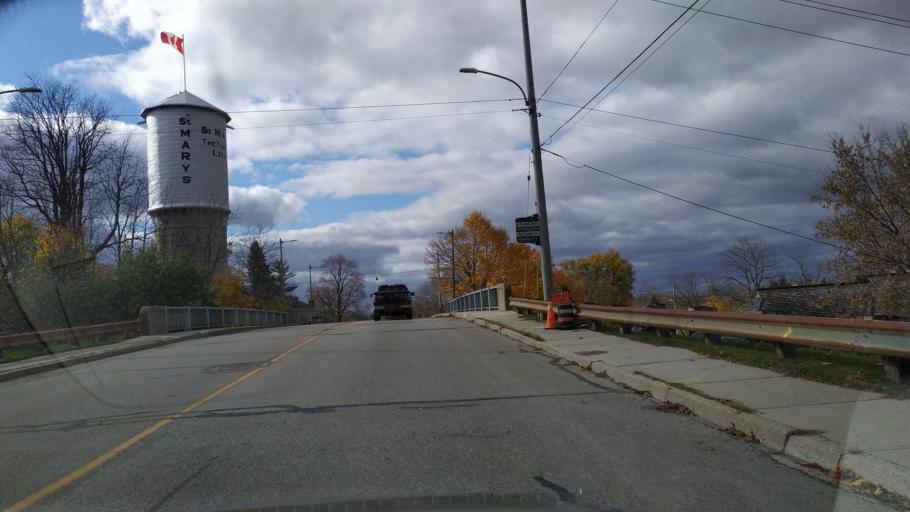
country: CA
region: Ontario
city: Stratford
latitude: 43.2601
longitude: -81.1358
